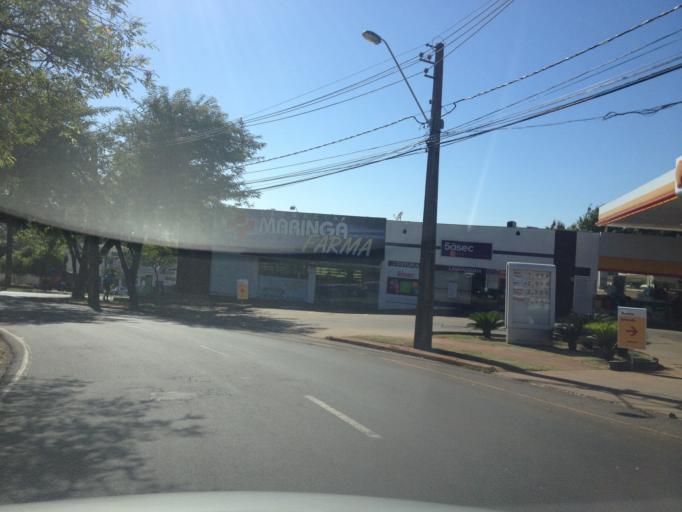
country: BR
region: Parana
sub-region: Maringa
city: Maringa
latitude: -23.4487
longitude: -51.9441
